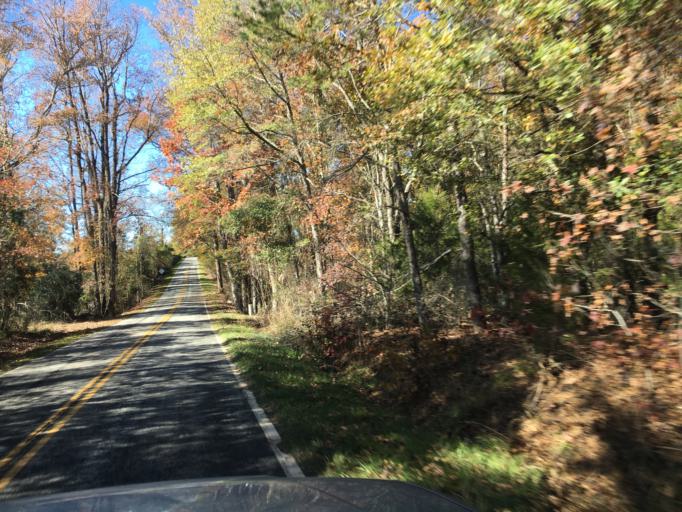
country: US
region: Georgia
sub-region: Hart County
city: Hartwell
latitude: 34.3895
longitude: -82.8019
